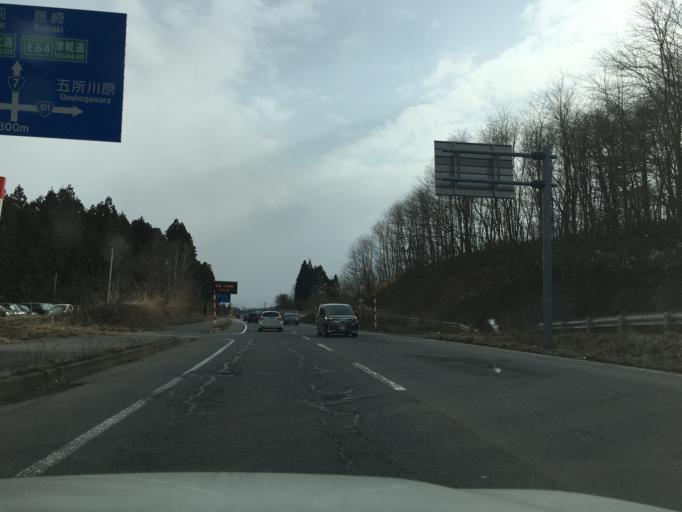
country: JP
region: Aomori
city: Namioka
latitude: 40.7630
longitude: 140.5875
